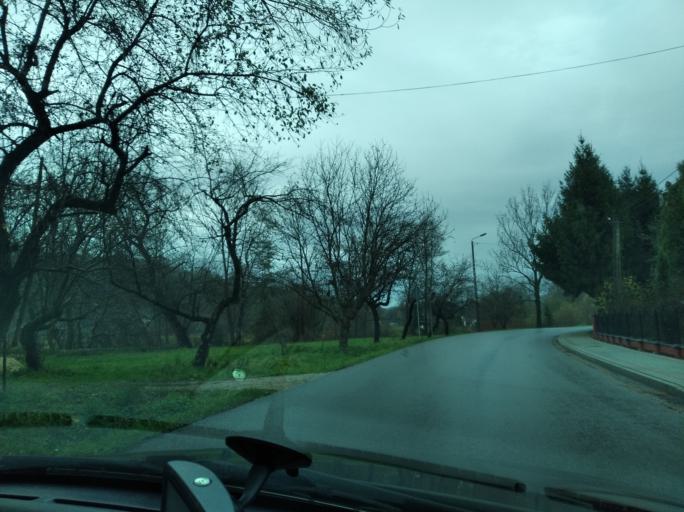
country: PL
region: Subcarpathian Voivodeship
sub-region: Powiat rzeszowski
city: Straszydle
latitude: 49.9169
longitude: 21.9577
